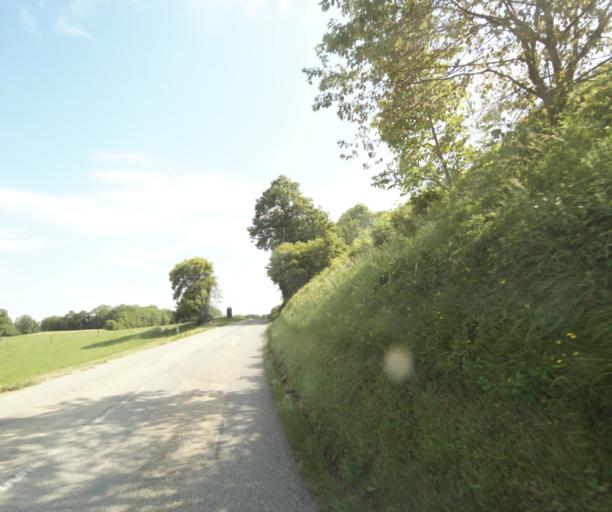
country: FR
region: Rhone-Alpes
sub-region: Departement de la Haute-Savoie
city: Lyaud
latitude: 46.3294
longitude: 6.5088
